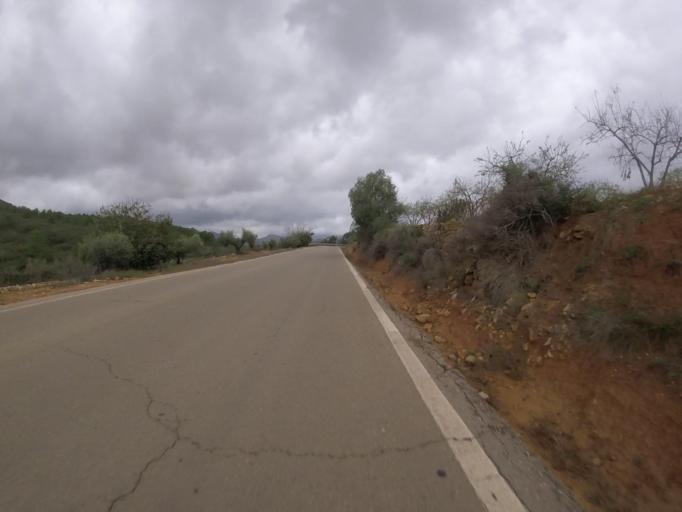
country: ES
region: Valencia
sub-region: Provincia de Castello
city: Cabanes
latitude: 40.1553
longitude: 0.0590
